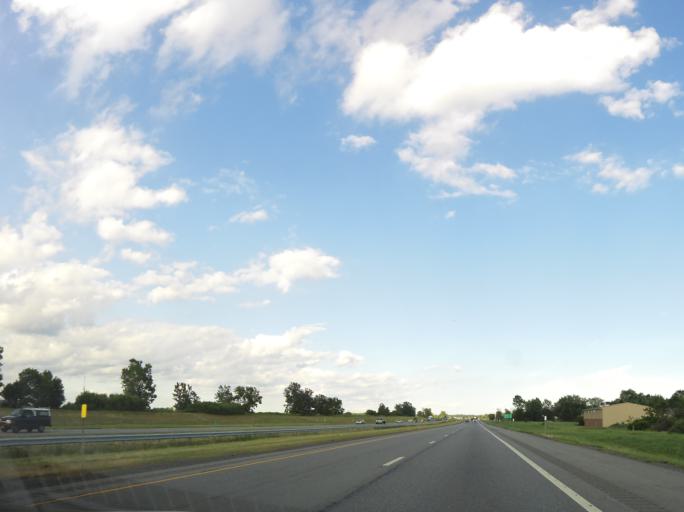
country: US
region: New York
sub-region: Erie County
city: Harris Hill
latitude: 42.9473
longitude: -78.6632
